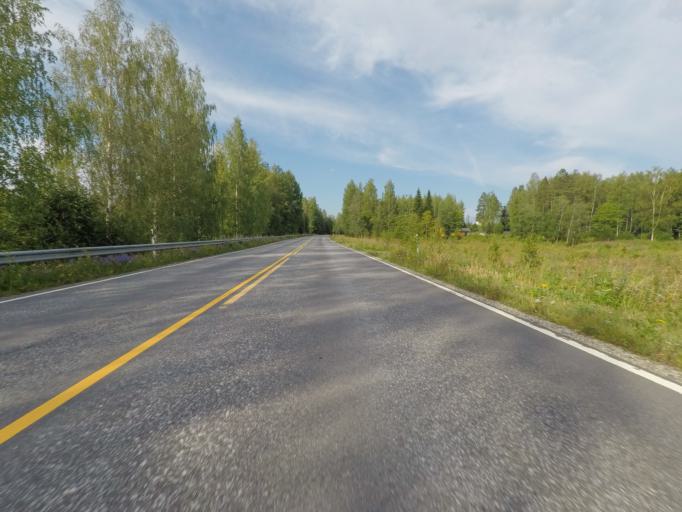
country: FI
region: Southern Savonia
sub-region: Savonlinna
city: Sulkava
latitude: 61.9018
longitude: 28.5842
